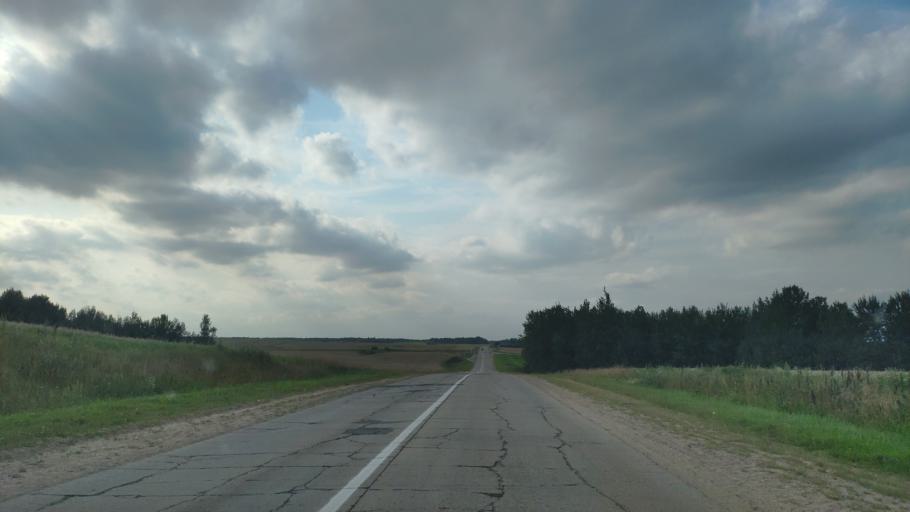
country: BY
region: Minsk
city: Khatsyezhyna
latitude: 53.8444
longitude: 27.2850
